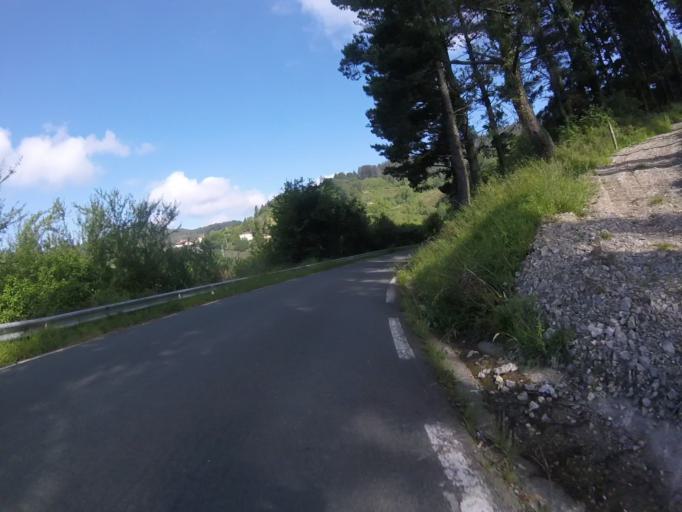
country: ES
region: Basque Country
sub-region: Provincia de Guipuzcoa
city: Ormaiztegui
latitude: 43.0823
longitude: -2.2341
